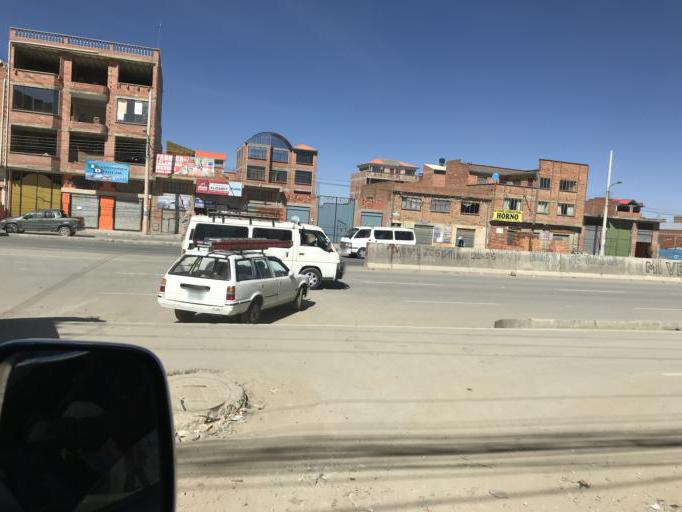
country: BO
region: La Paz
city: La Paz
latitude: -16.4890
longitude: -68.2113
